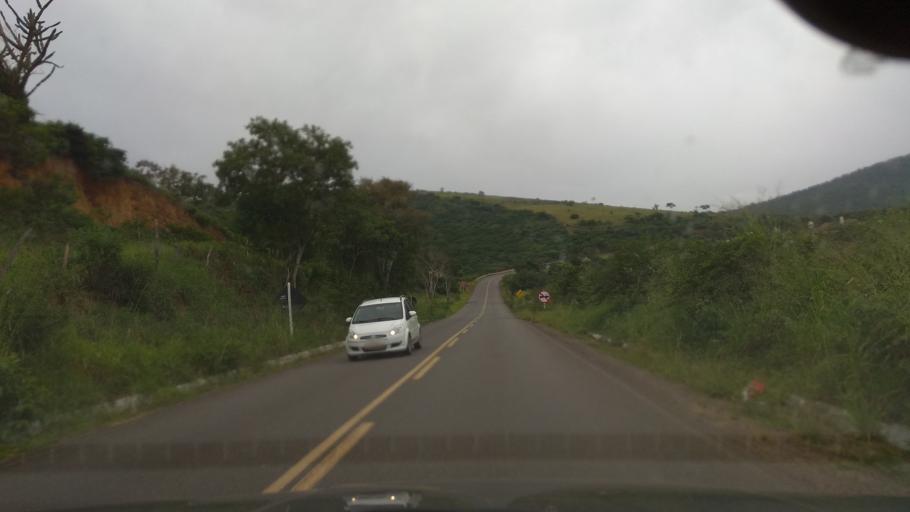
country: BR
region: Bahia
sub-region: Santa Ines
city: Santa Ines
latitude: -13.2404
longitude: -39.7531
